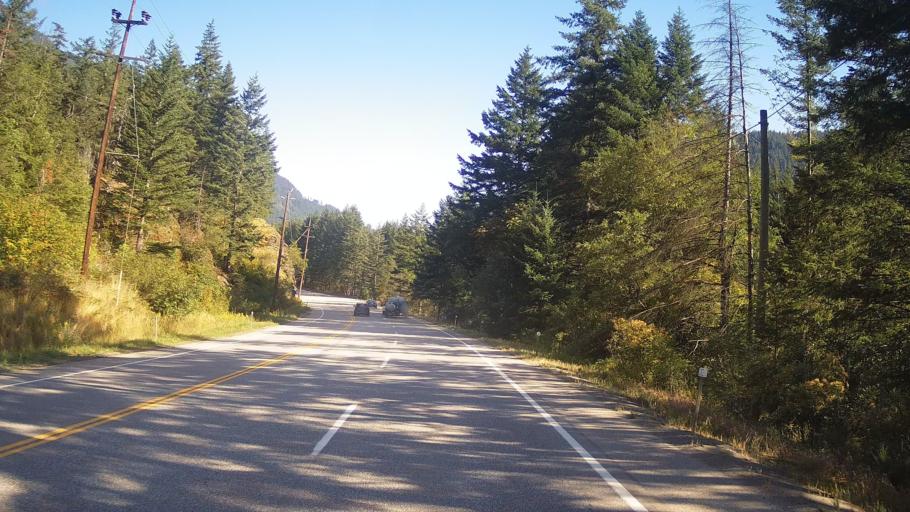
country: CA
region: British Columbia
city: Hope
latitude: 49.6554
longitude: -121.4058
